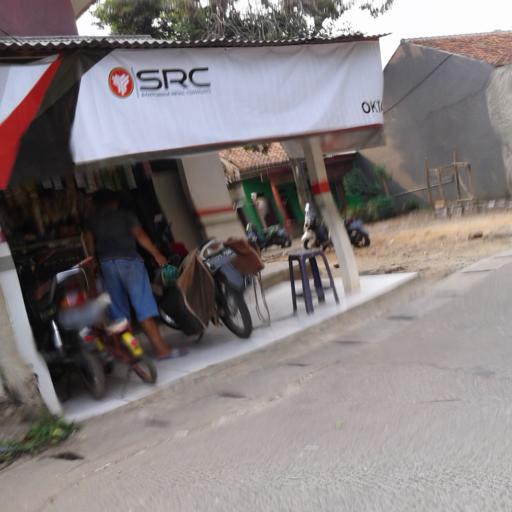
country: ID
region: West Java
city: Sawangan
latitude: -6.4043
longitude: 106.7652
